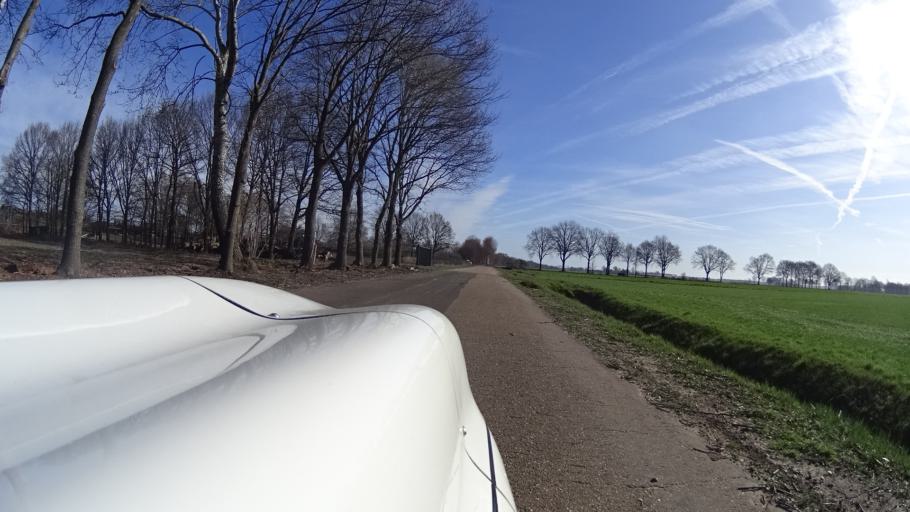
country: NL
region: North Brabant
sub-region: Gemeente Uden
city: Odiliapeel
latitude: 51.6688
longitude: 5.7076
